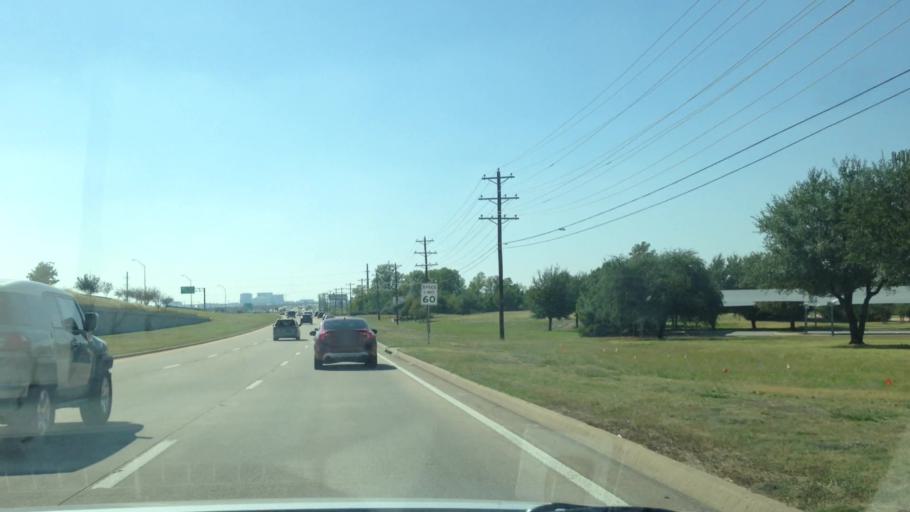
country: US
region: Texas
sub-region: Collin County
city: Frisco
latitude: 33.1128
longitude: -96.7688
